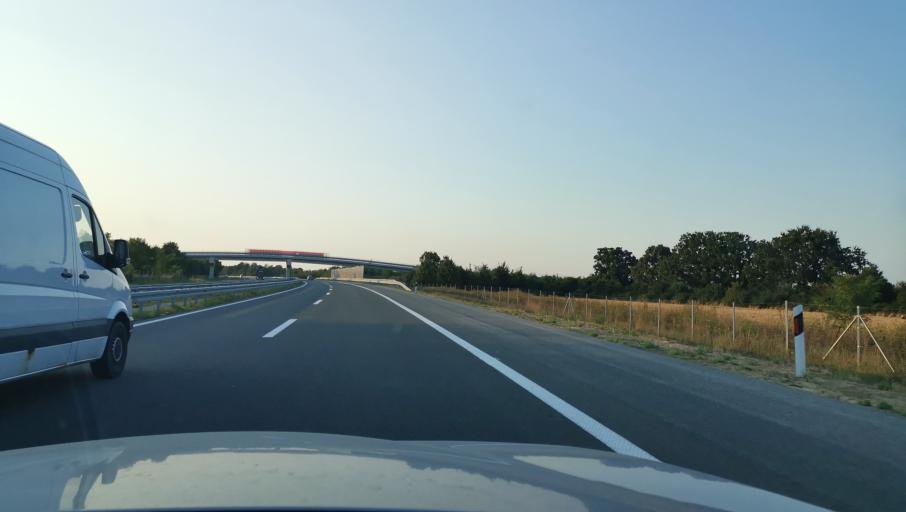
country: RS
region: Central Serbia
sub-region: Kolubarski Okrug
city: Lajkovac
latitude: 44.3766
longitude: 20.1173
